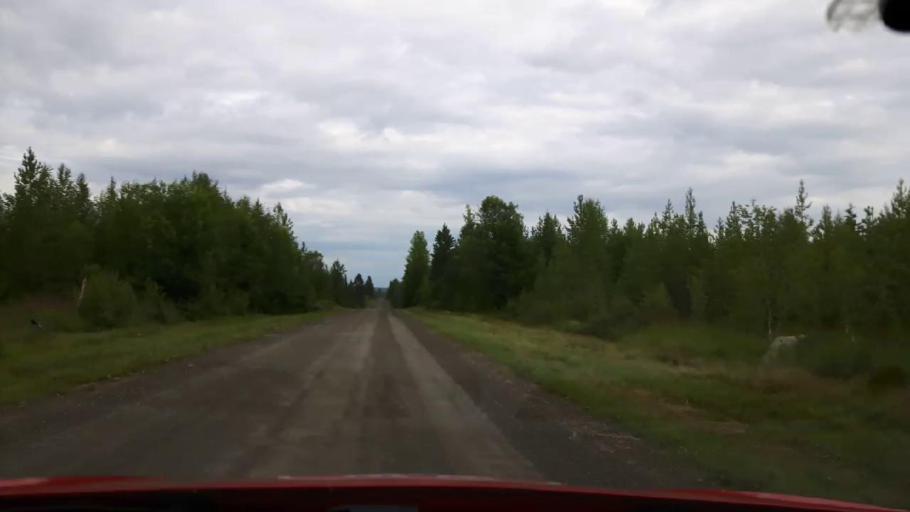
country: SE
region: Jaemtland
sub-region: Stroemsunds Kommun
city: Stroemsund
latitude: 63.7907
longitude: 15.6162
